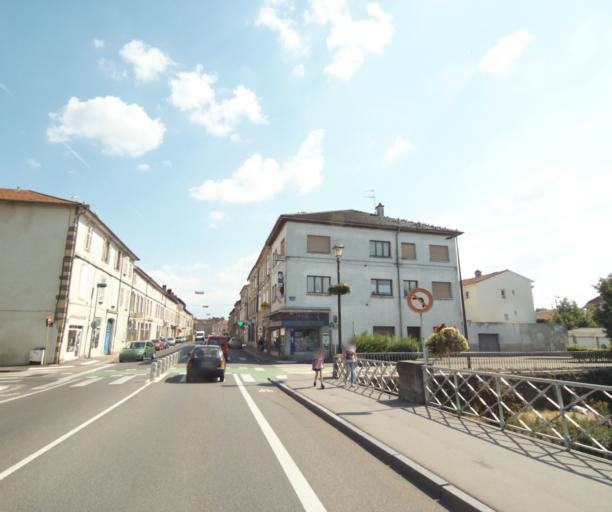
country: FR
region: Lorraine
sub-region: Departement de Meurthe-et-Moselle
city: Luneville
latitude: 48.5971
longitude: 6.4892
